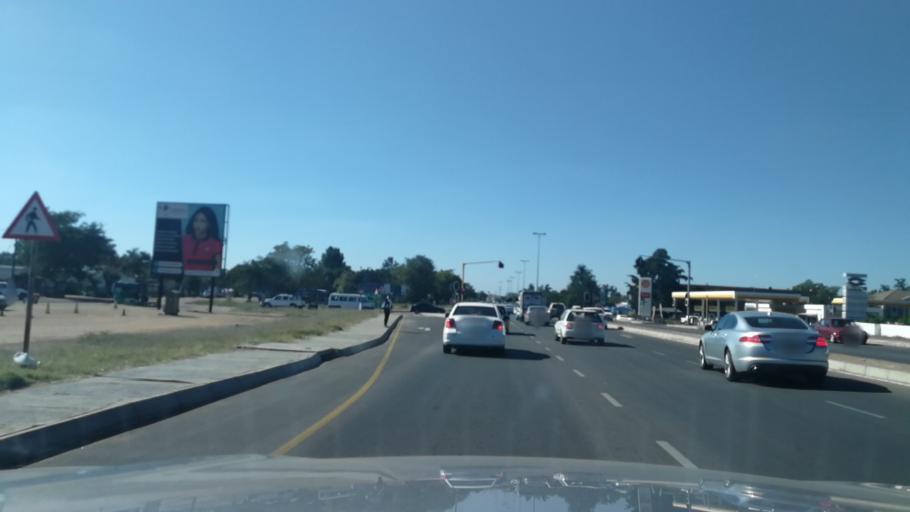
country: BW
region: South East
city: Gaborone
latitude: -24.6780
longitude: 25.9190
